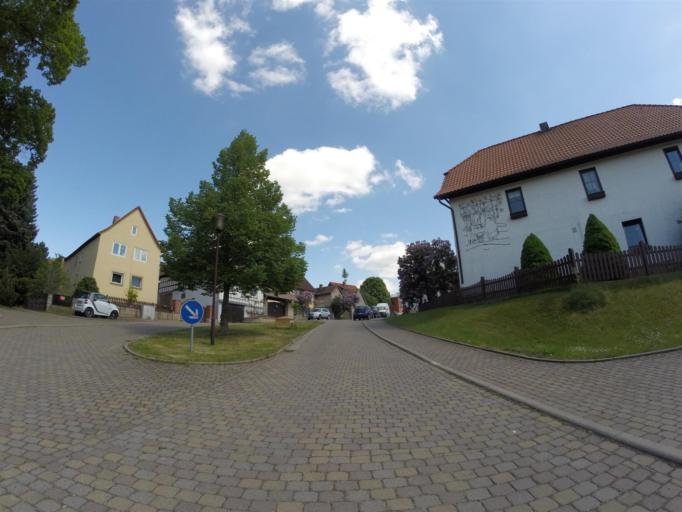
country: DE
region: Thuringia
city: Golmsdorf
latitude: 50.9737
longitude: 11.6722
